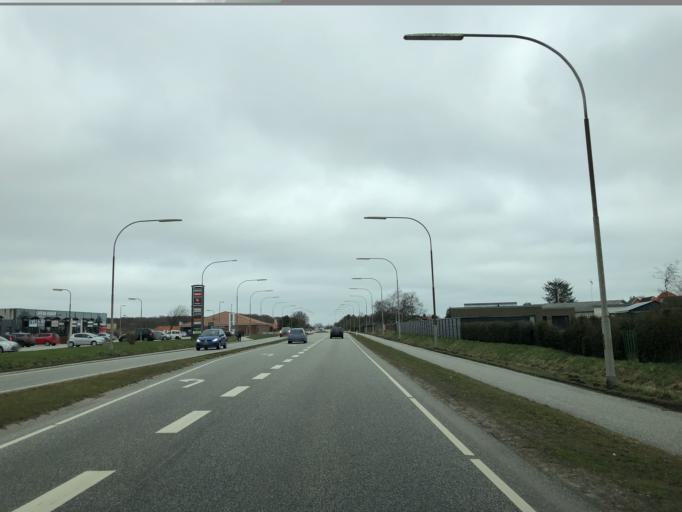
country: DK
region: North Denmark
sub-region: Frederikshavn Kommune
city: Saeby
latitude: 57.3303
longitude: 10.5040
